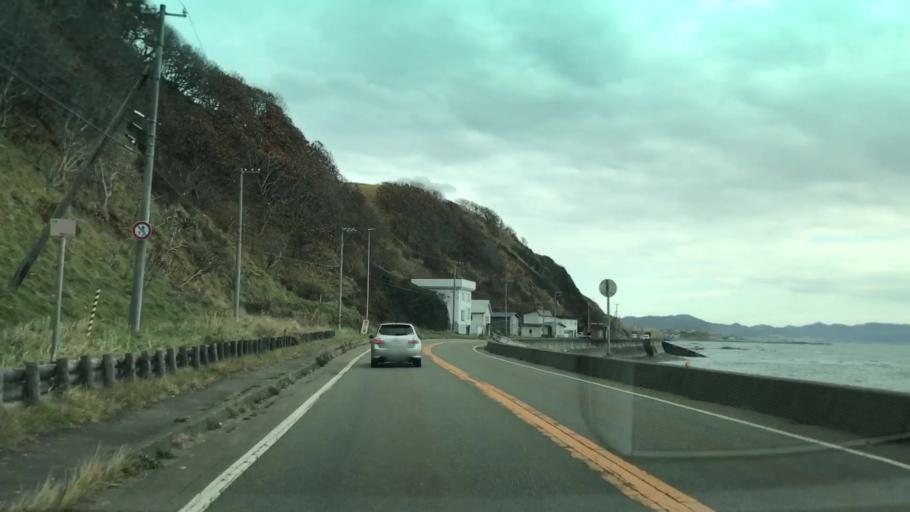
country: JP
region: Hokkaido
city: Shizunai-furukawacho
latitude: 42.0556
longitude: 143.0813
